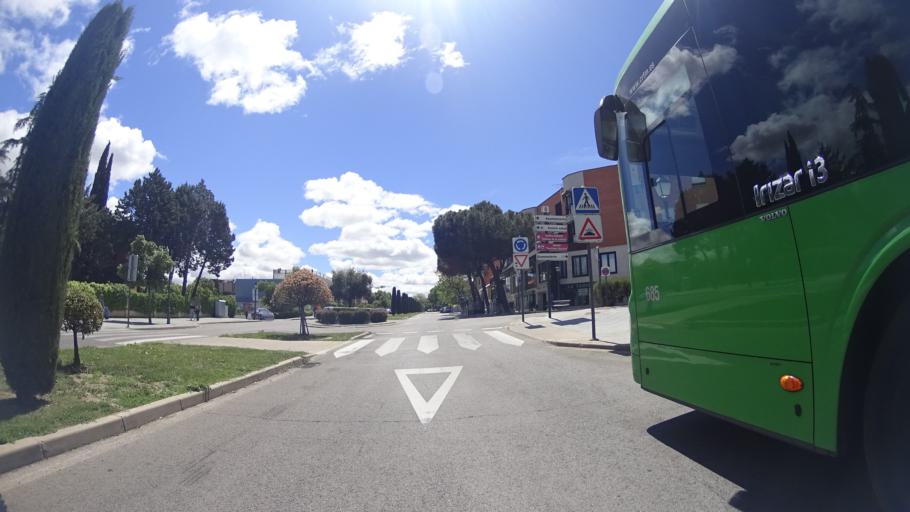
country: ES
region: Madrid
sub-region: Provincia de Madrid
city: Villaviciosa de Odon
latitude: 40.3605
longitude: -3.9097
